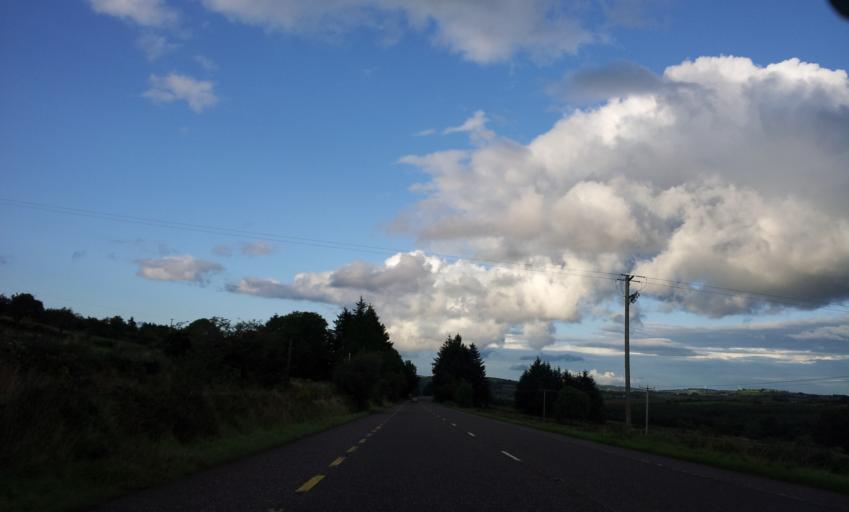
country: IE
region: Munster
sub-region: Ciarrai
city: Castleisland
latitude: 52.2913
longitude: -9.3983
